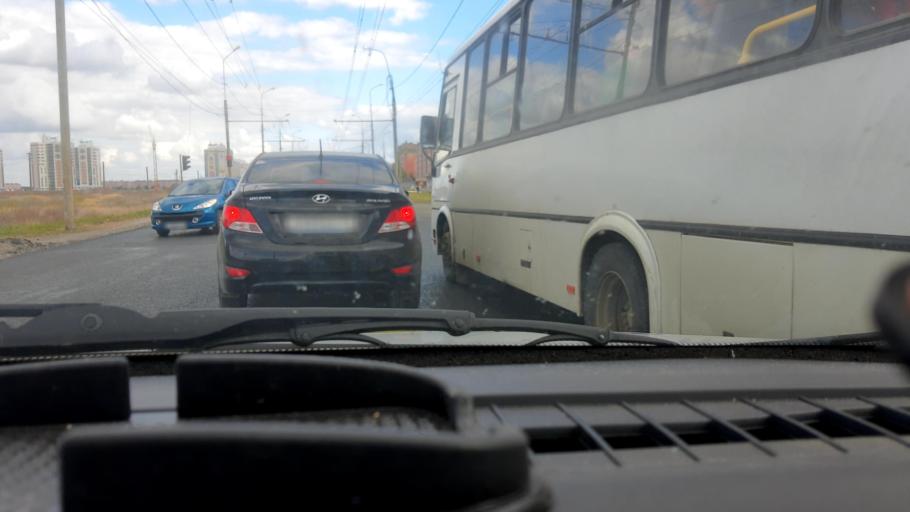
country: RU
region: Mariy-El
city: Medvedevo
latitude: 56.6388
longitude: 47.7916
